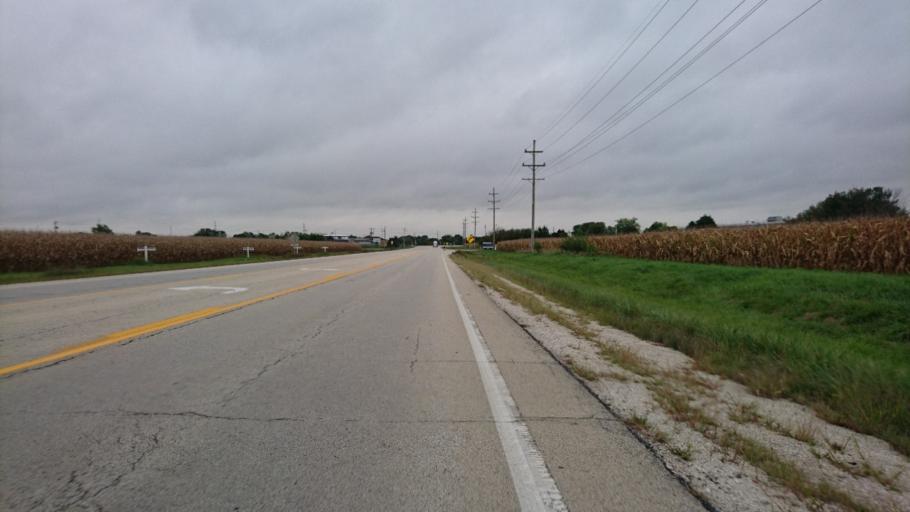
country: US
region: Illinois
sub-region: Livingston County
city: Dwight
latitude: 41.1087
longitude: -88.4136
